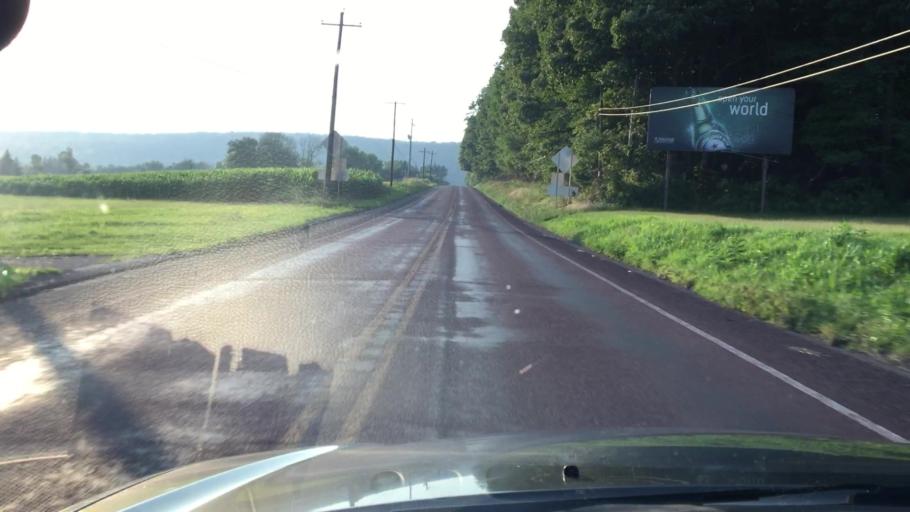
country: US
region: Pennsylvania
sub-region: Carbon County
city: Weatherly
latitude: 40.9201
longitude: -75.8597
